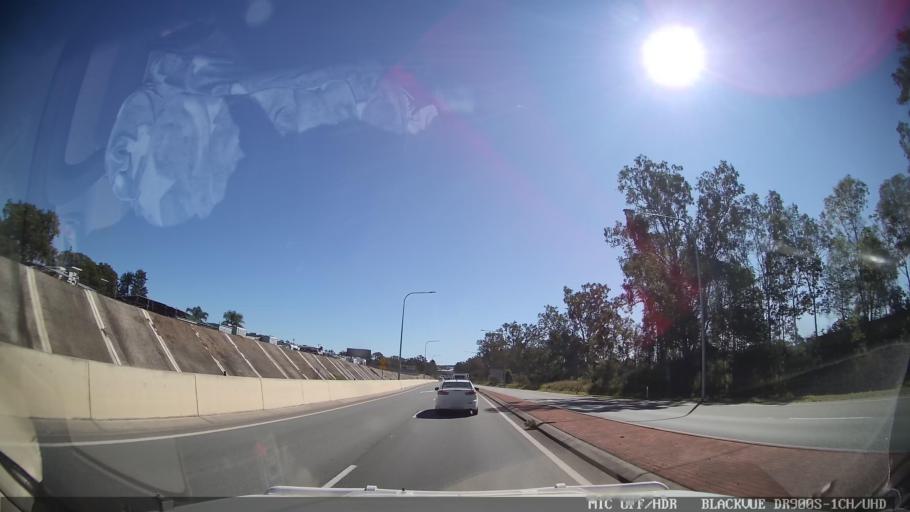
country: AU
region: Queensland
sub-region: Gympie Regional Council
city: Monkland
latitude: -26.2372
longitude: 152.6992
